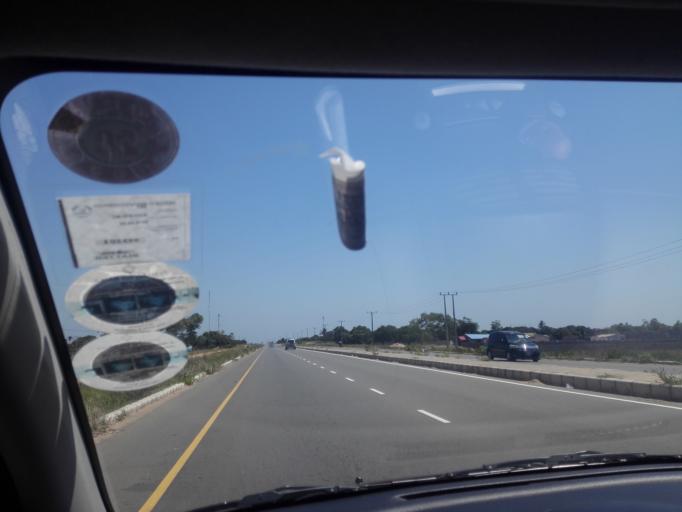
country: MZ
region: Maputo City
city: Maputo
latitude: -25.8169
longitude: 32.6727
